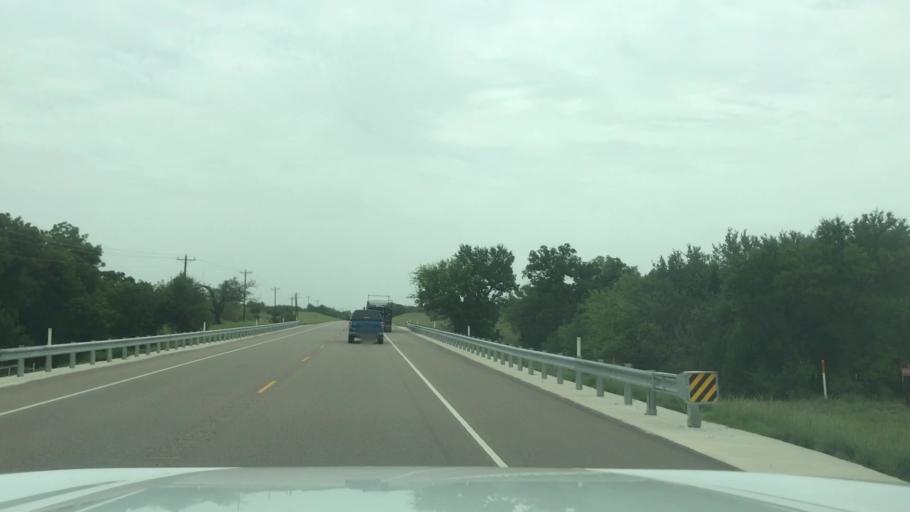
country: US
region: Texas
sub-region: Bosque County
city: Meridian
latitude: 31.9277
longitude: -97.6876
